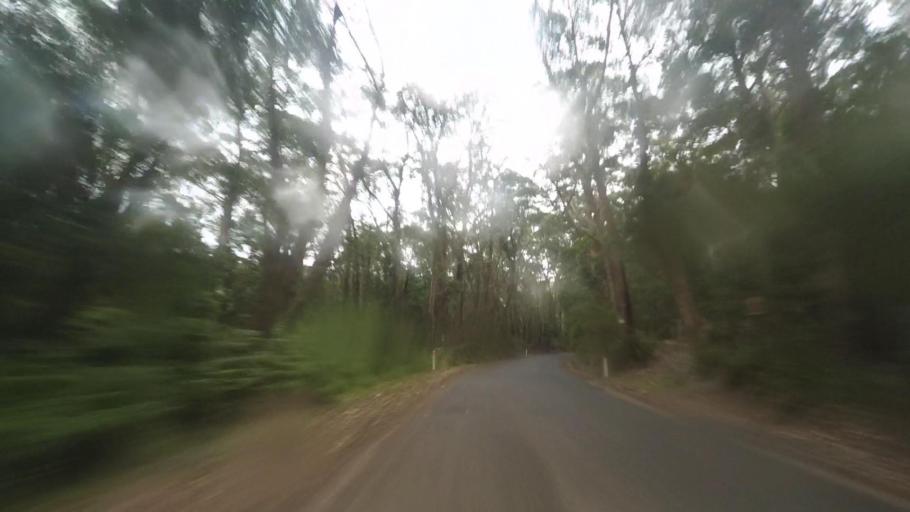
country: AU
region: New South Wales
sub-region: Wollongong
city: Cordeaux Heights
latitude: -34.4072
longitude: 150.8168
